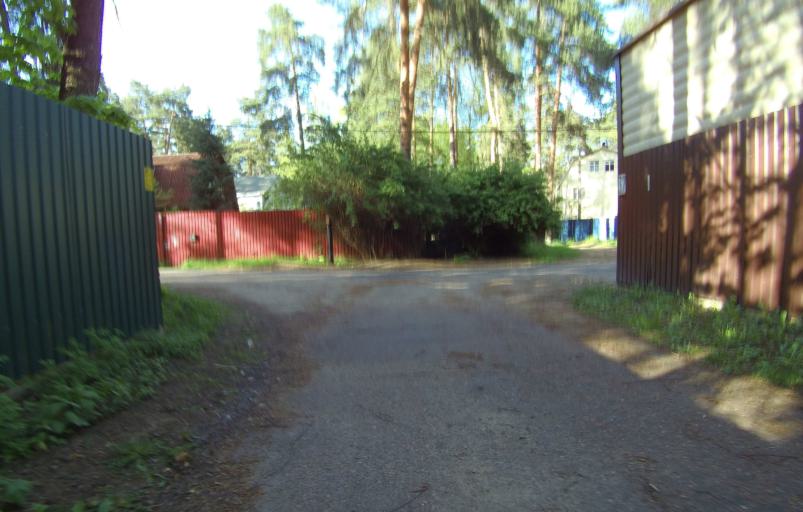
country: RU
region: Moskovskaya
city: Kratovo
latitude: 55.5918
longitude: 38.1663
